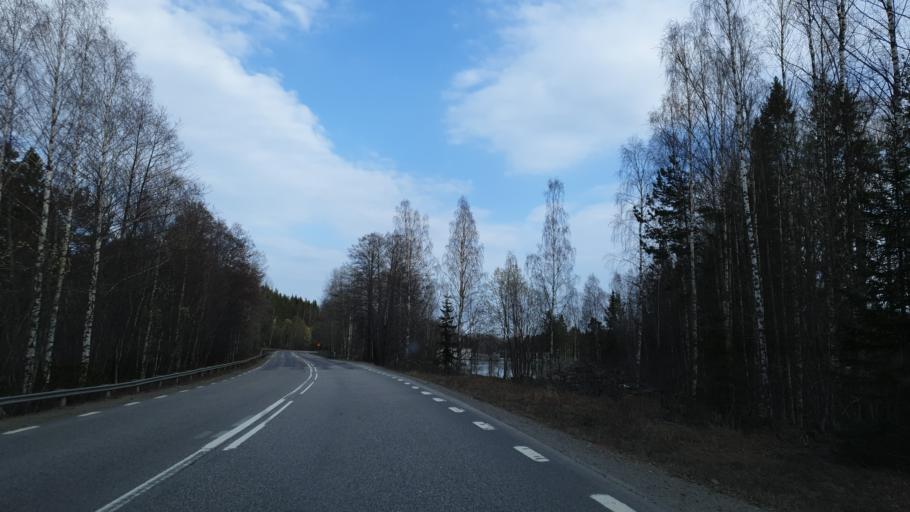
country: SE
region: Gaevleborg
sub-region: Hudiksvalls Kommun
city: Iggesund
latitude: 61.6505
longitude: 17.0328
